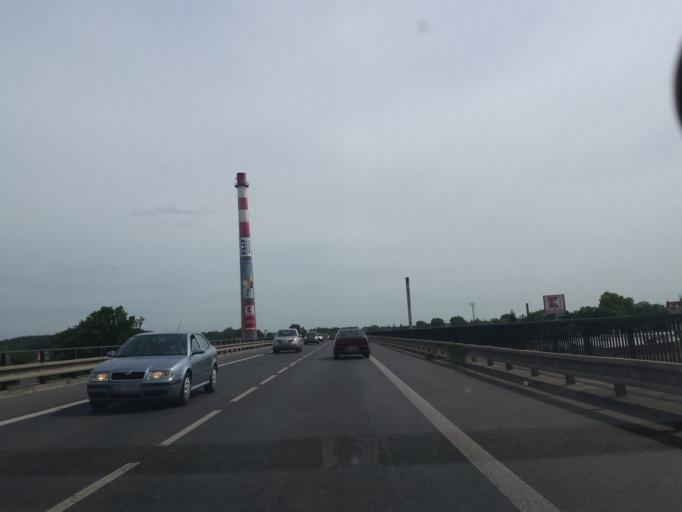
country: CZ
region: Liberecky
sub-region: Okres Ceska Lipa
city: Ceska Lipa
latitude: 50.6819
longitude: 14.5415
